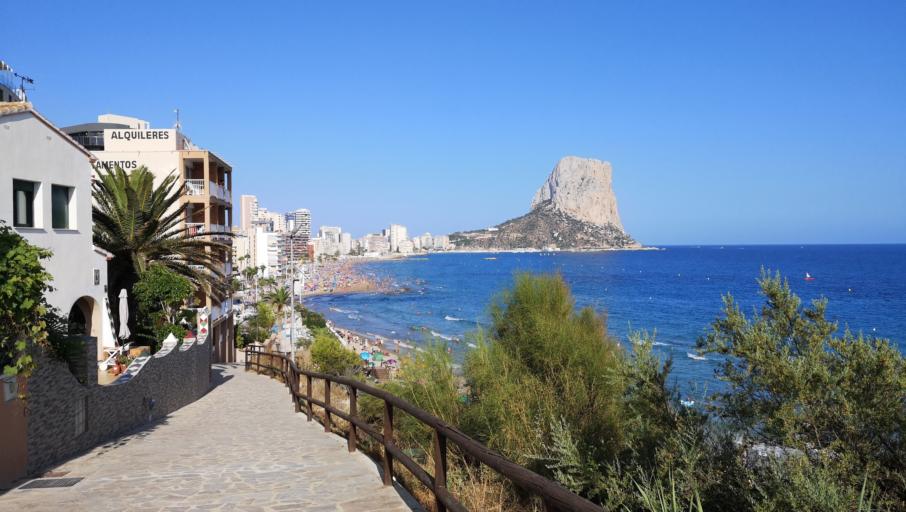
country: ES
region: Valencia
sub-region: Provincia de Alicante
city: Calp
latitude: 38.6416
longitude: 0.0471
